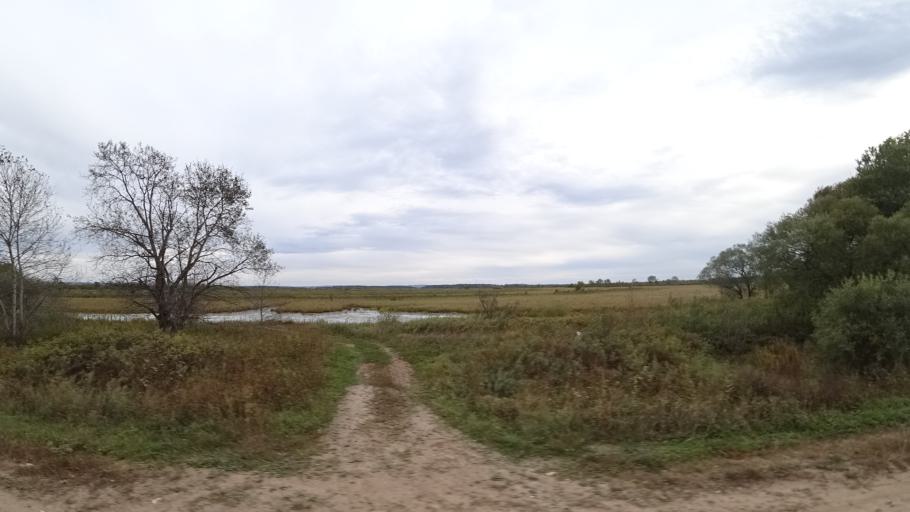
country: RU
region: Amur
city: Arkhara
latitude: 49.4306
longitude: 130.2371
